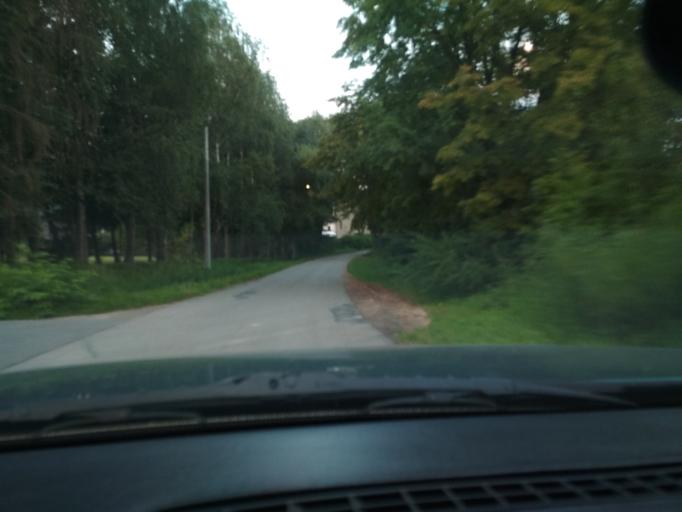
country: PL
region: Silesian Voivodeship
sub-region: Powiat bielski
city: Jasienica
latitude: 49.8387
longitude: 18.9365
